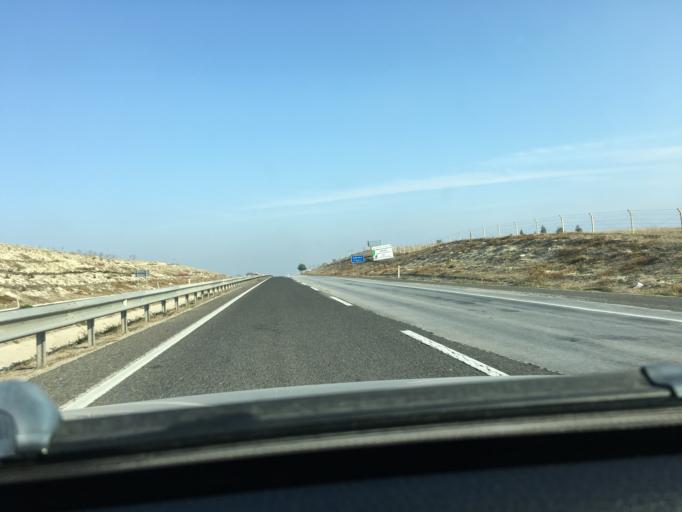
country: TR
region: Eskisehir
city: Gunyuzu
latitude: 39.5751
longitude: 31.8942
